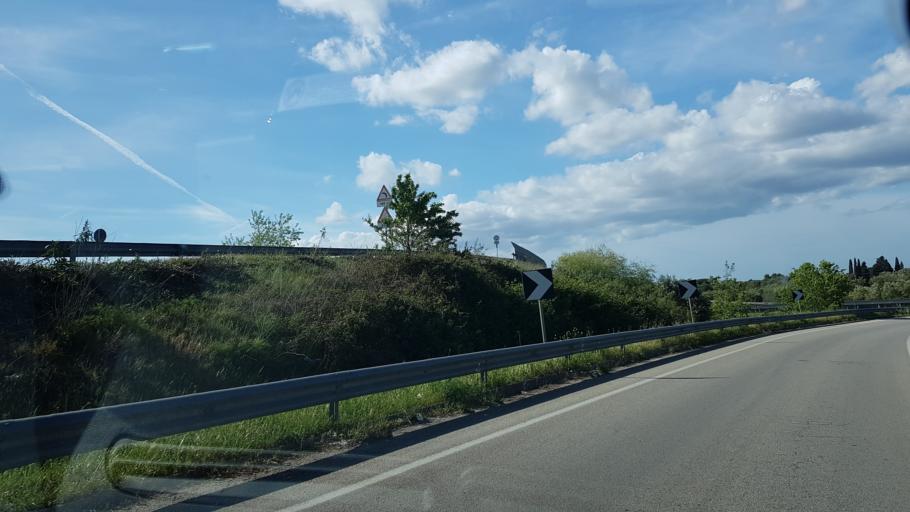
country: IT
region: Apulia
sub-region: Provincia di Brindisi
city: Mesagne
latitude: 40.5667
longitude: 17.7862
